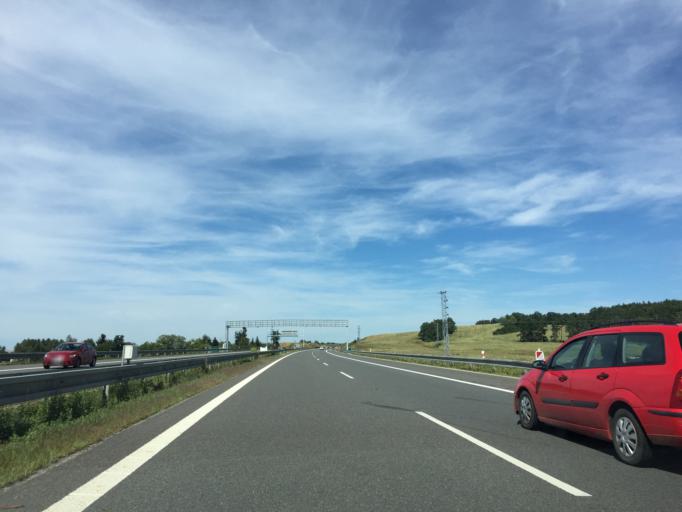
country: CZ
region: Jihocesky
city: Sobeslav
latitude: 49.2456
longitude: 14.7296
